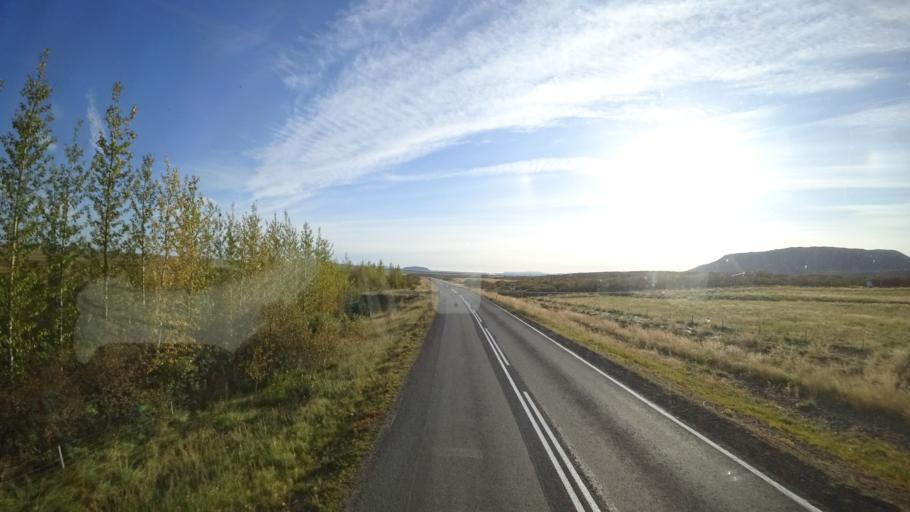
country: IS
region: South
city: Selfoss
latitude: 64.2649
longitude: -20.4674
